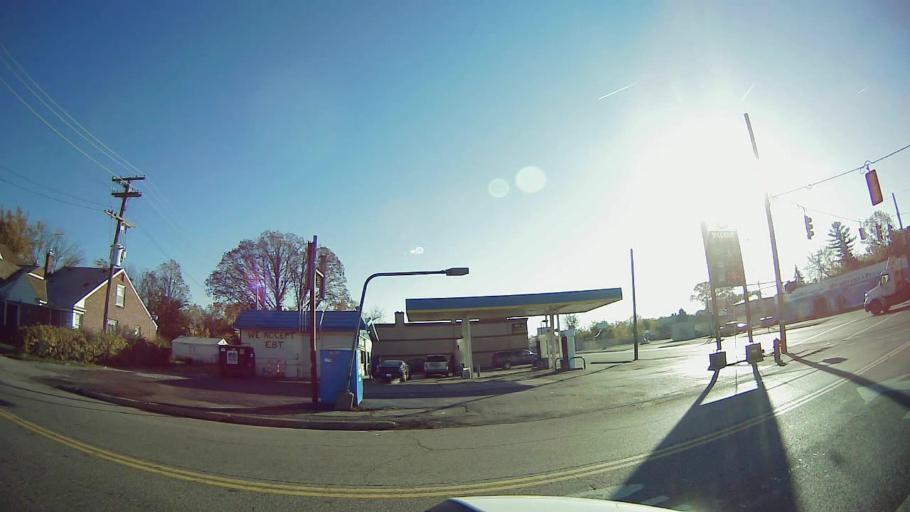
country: US
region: Michigan
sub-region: Wayne County
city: Dearborn
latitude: 42.3589
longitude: -83.1678
